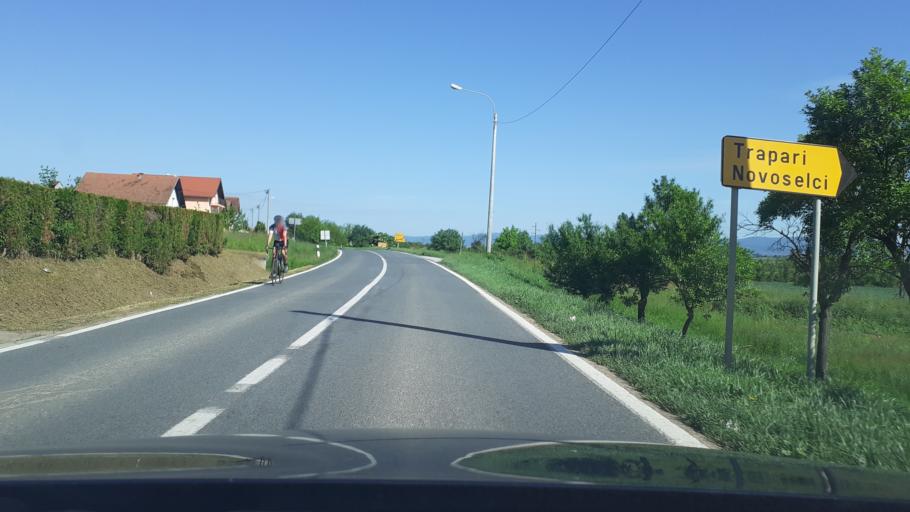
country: HR
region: Pozesko-Slavonska
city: Jaksic
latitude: 45.3191
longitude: 17.7727
